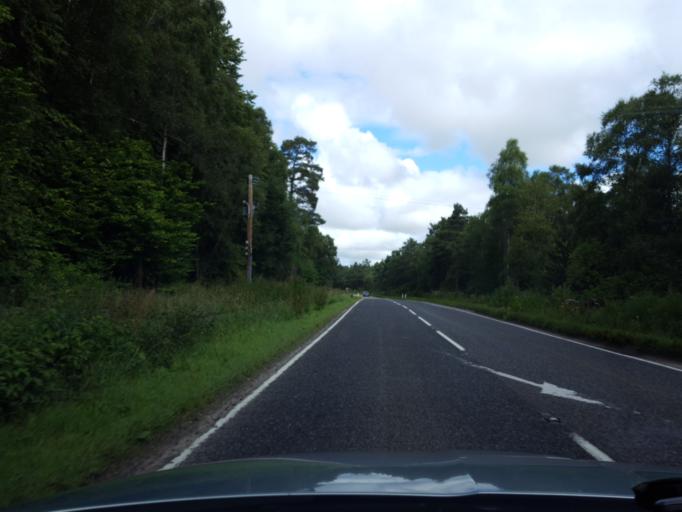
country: GB
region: Scotland
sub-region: Moray
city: Rothes
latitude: 57.5593
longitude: -3.2460
